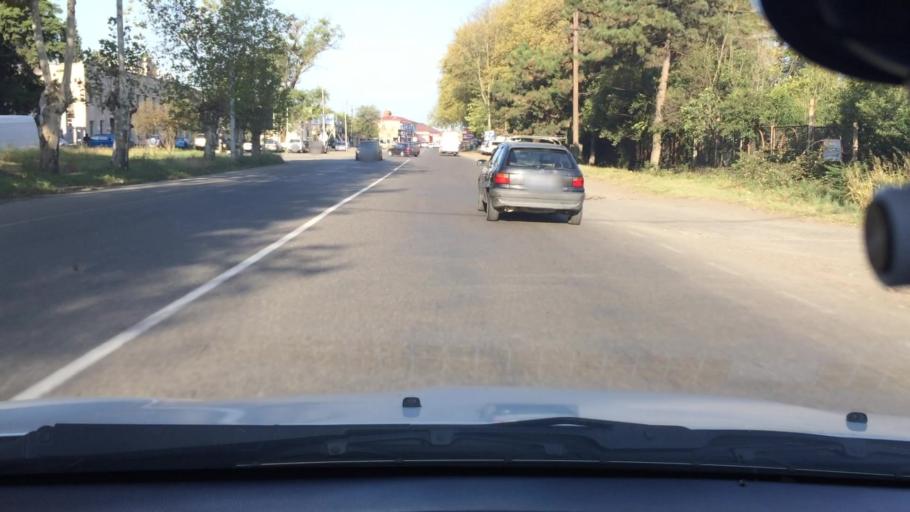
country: GE
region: Imereti
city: Zestap'oni
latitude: 42.1188
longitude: 43.0149
